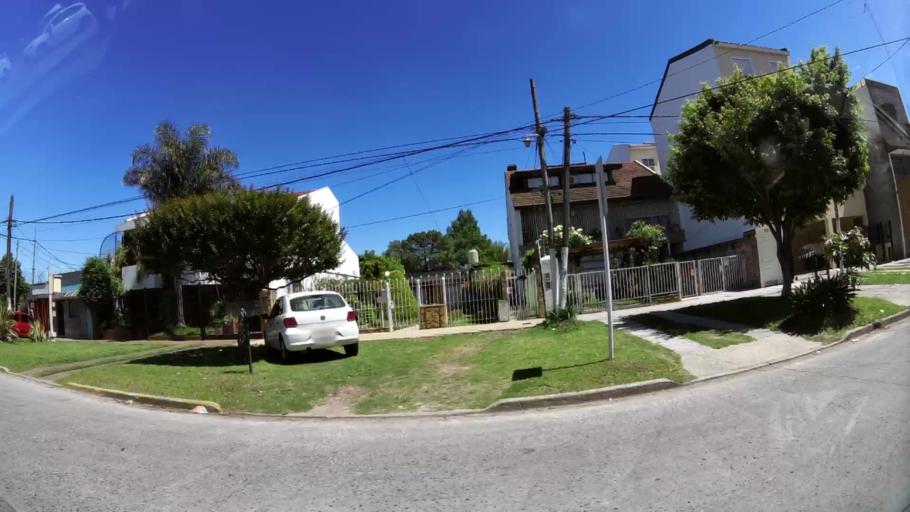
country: AR
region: Buenos Aires
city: Caseros
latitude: -34.5944
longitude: -58.5686
